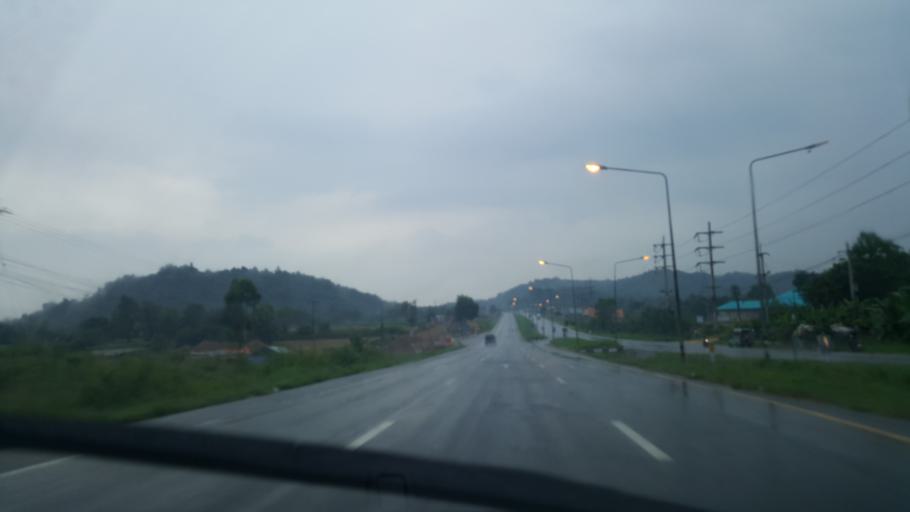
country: TH
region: Chon Buri
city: Ban Talat Bueng
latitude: 13.0017
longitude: 101.0647
